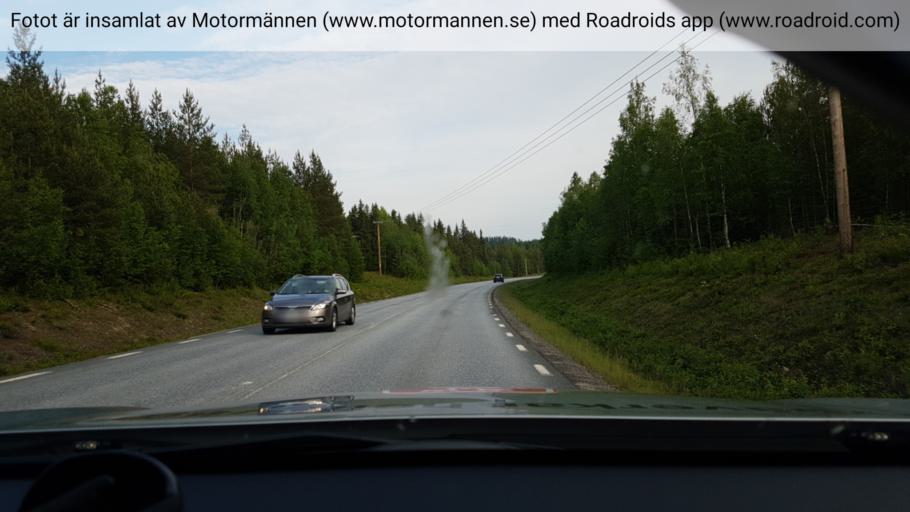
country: SE
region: Vaesterbotten
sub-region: Vannas Kommun
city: Vaennaes
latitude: 63.9449
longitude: 19.7669
